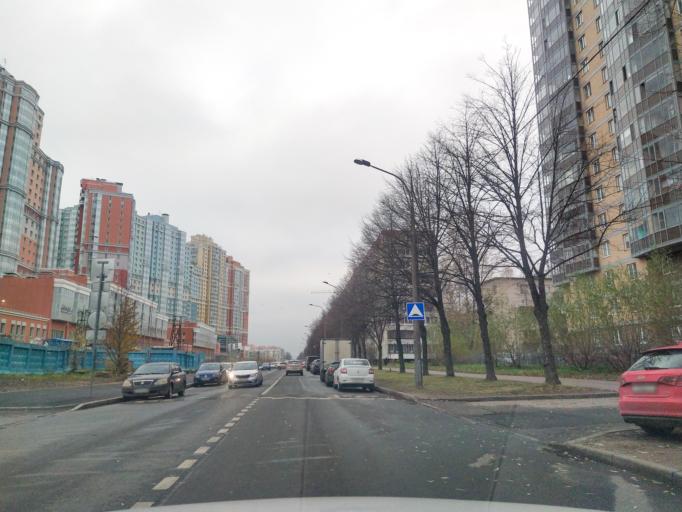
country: RU
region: St.-Petersburg
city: Sosnovka
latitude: 60.0418
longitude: 30.3627
